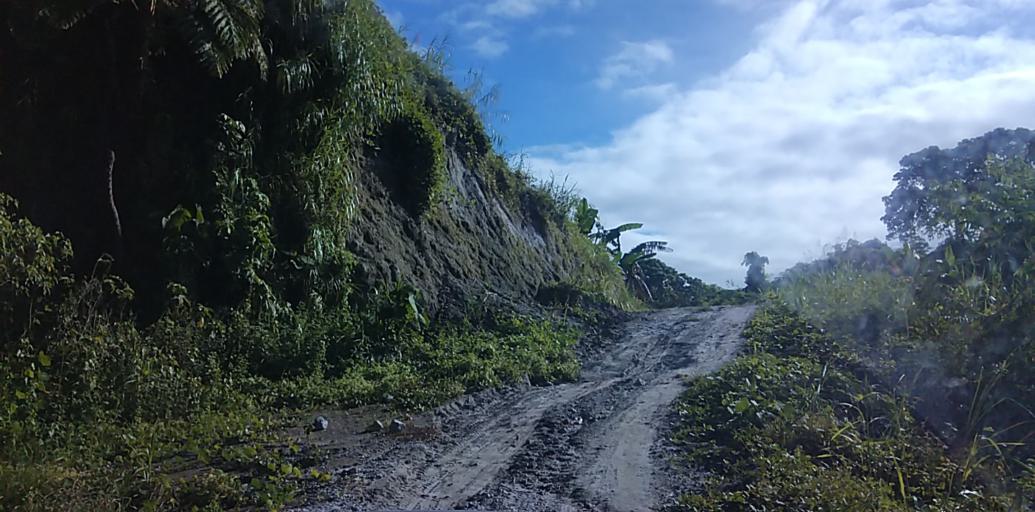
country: PH
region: Central Luzon
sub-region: Province of Pampanga
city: Babo-Pangulo
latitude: 15.1503
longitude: 120.4437
